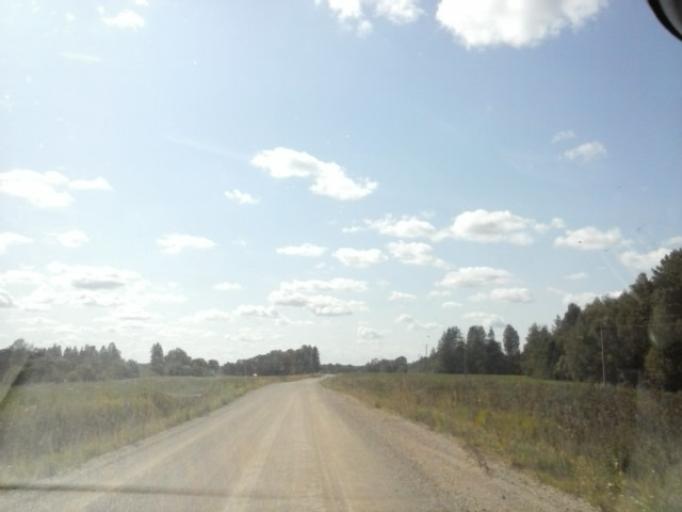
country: EE
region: Polvamaa
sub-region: Polva linn
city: Polva
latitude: 58.1044
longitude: 26.8542
